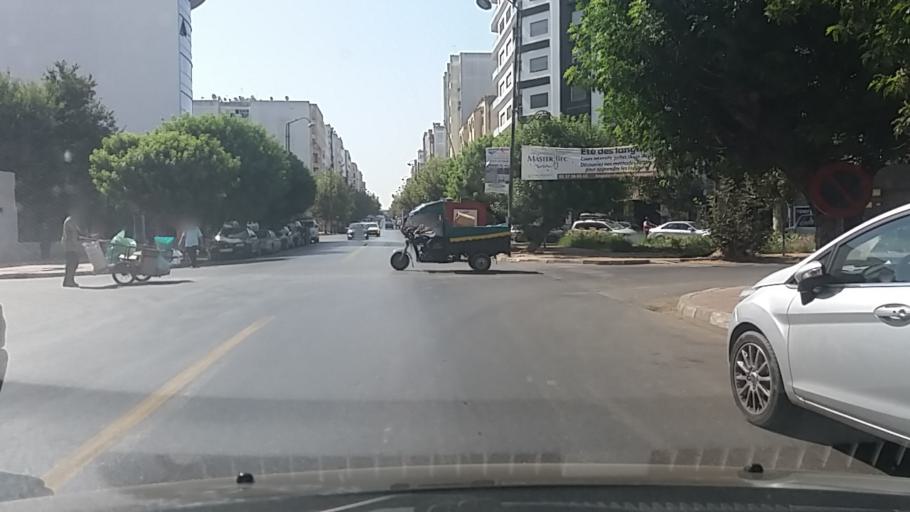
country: MA
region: Gharb-Chrarda-Beni Hssen
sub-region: Kenitra Province
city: Kenitra
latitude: 34.2576
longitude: -6.5834
